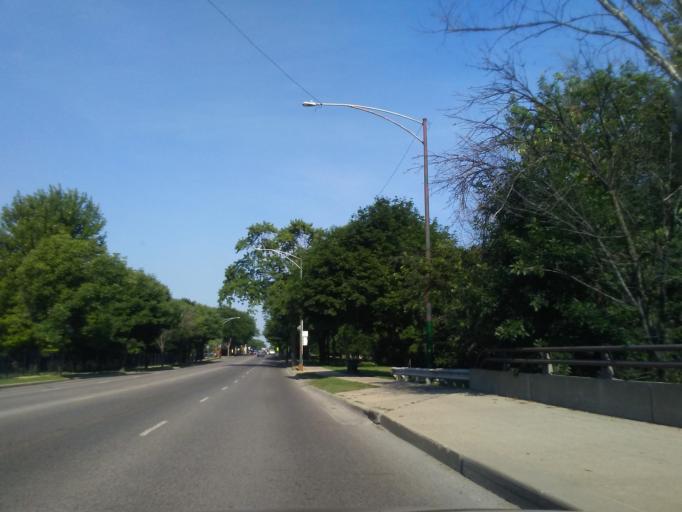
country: US
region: Illinois
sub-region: Cook County
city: Lincolnwood
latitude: 41.9756
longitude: -87.7312
